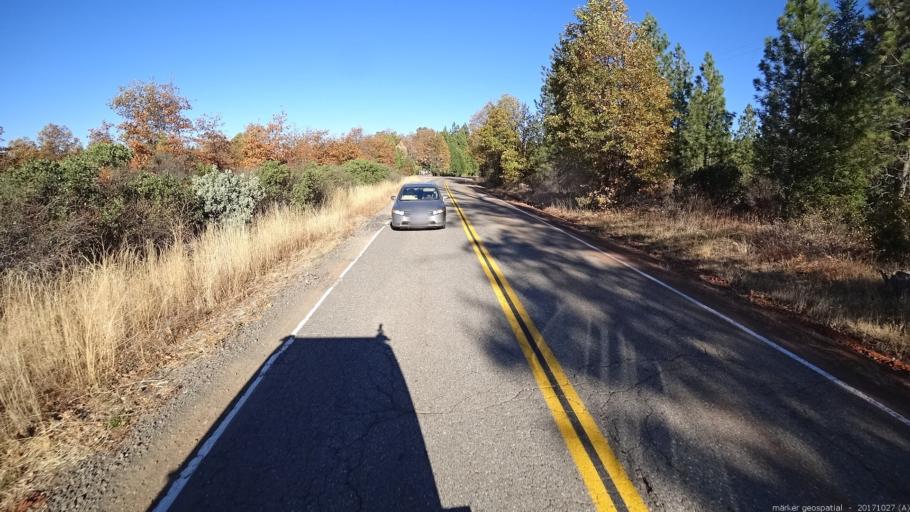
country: US
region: California
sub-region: Shasta County
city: Burney
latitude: 40.8758
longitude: -121.9070
